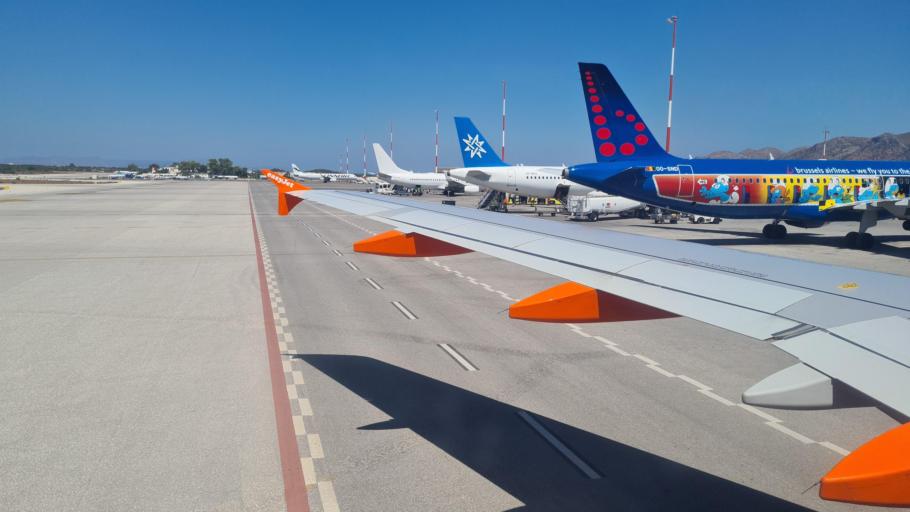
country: GR
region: Crete
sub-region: Nomos Chanias
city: Mouzouras
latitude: 35.5374
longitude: 24.1431
